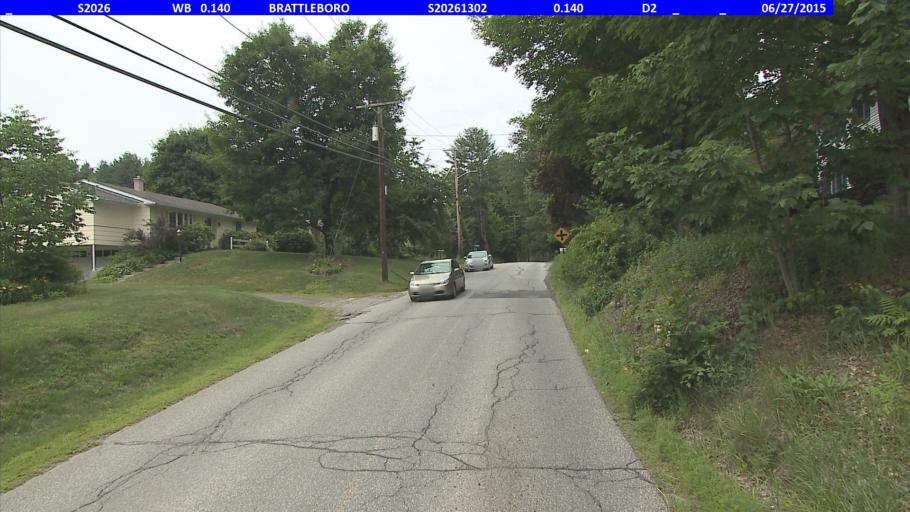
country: US
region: Vermont
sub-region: Windham County
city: West Brattleboro
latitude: 42.8552
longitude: -72.6069
